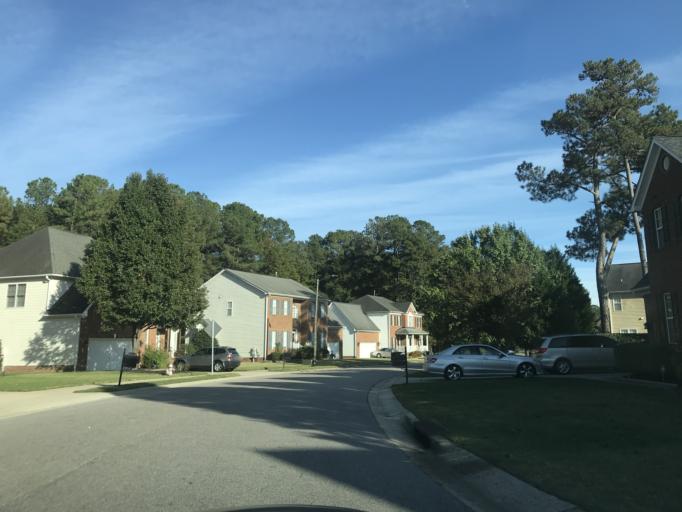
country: US
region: North Carolina
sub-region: Wake County
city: Rolesville
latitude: 35.8923
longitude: -78.5423
